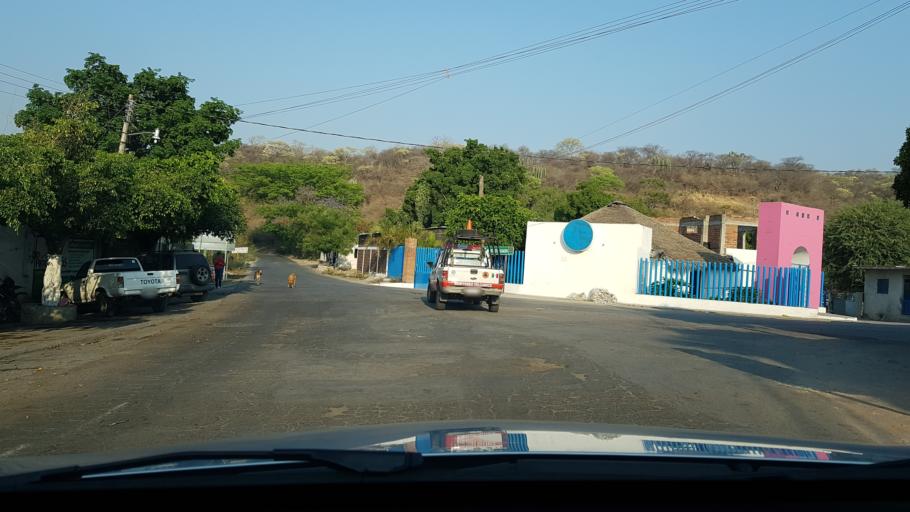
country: MX
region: Morelos
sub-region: Tepalcingo
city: Zacapalco
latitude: 18.6381
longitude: -99.0084
